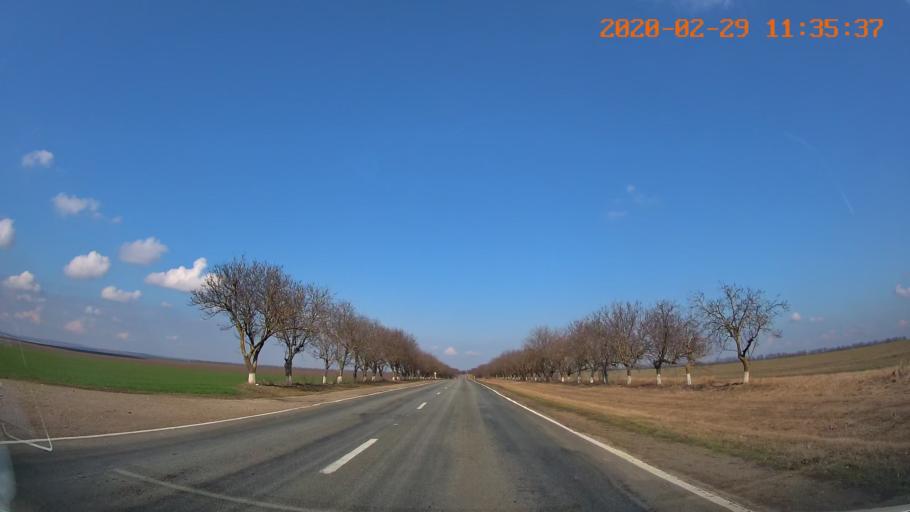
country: MD
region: Rezina
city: Saharna
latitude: 47.5831
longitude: 29.0622
